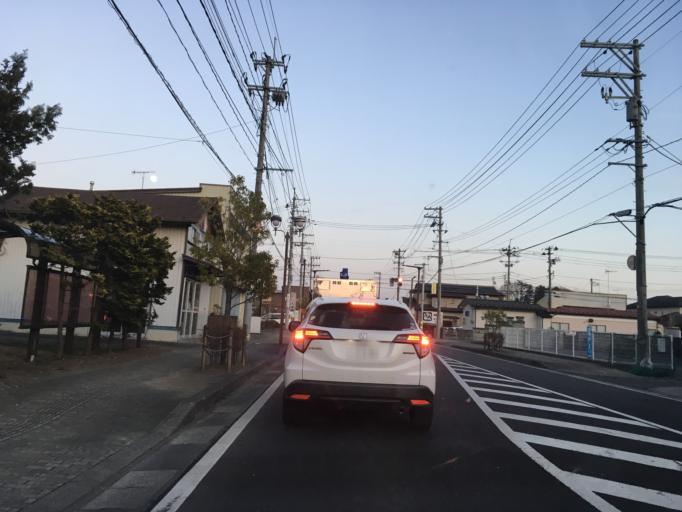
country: JP
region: Miyagi
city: Wakuya
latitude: 38.6853
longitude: 141.1938
